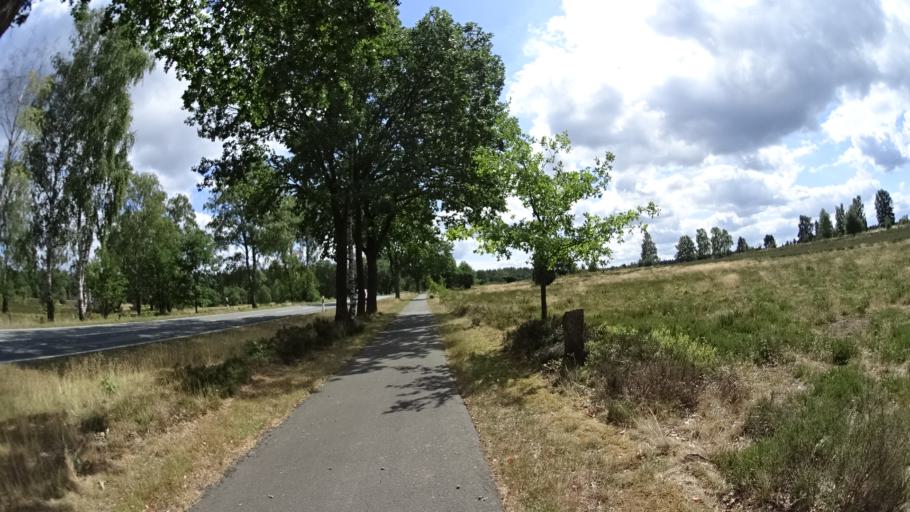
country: DE
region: Lower Saxony
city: Undeloh
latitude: 53.2152
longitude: 9.9475
